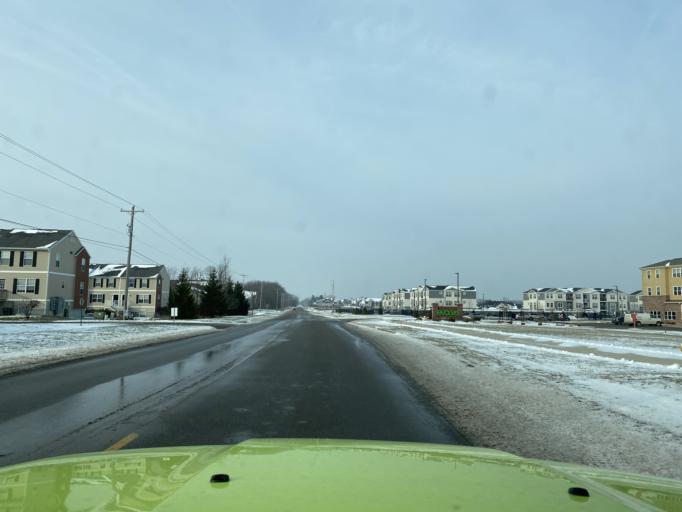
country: US
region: Michigan
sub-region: Ottawa County
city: Allendale
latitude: 42.9578
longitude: -85.9069
